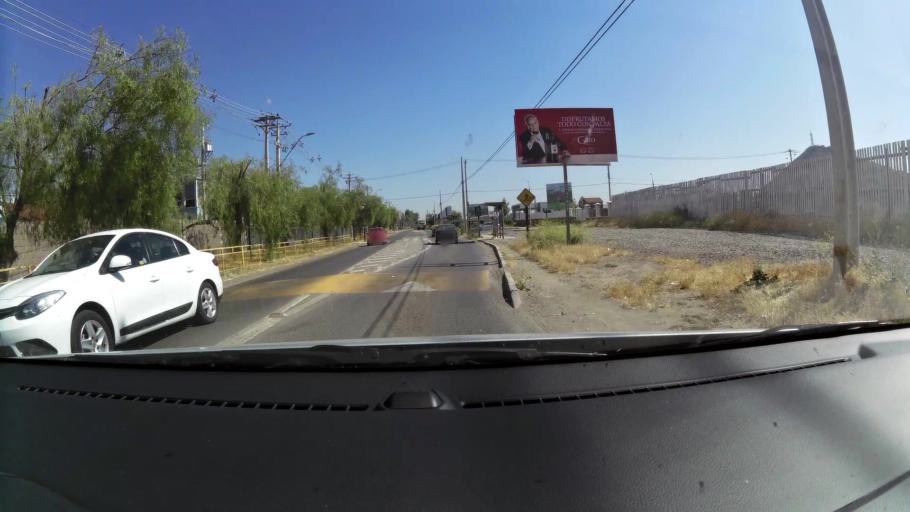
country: CL
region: Santiago Metropolitan
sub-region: Provincia de Maipo
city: San Bernardo
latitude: -33.6196
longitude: -70.6816
